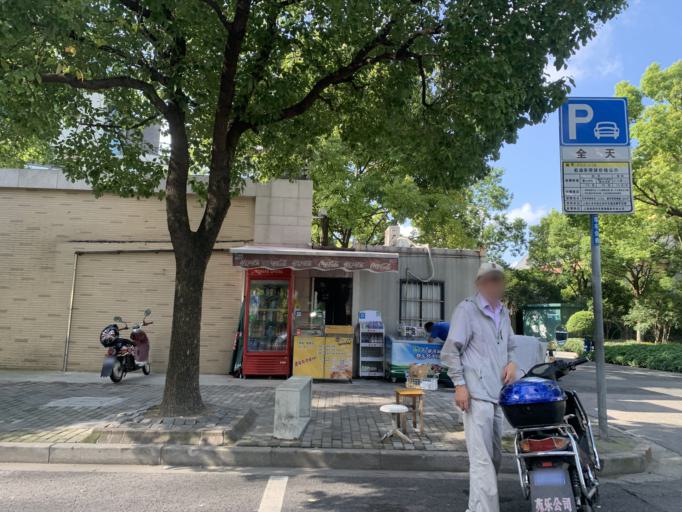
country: CN
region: Shanghai Shi
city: Pudong
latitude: 31.2263
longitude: 121.5047
